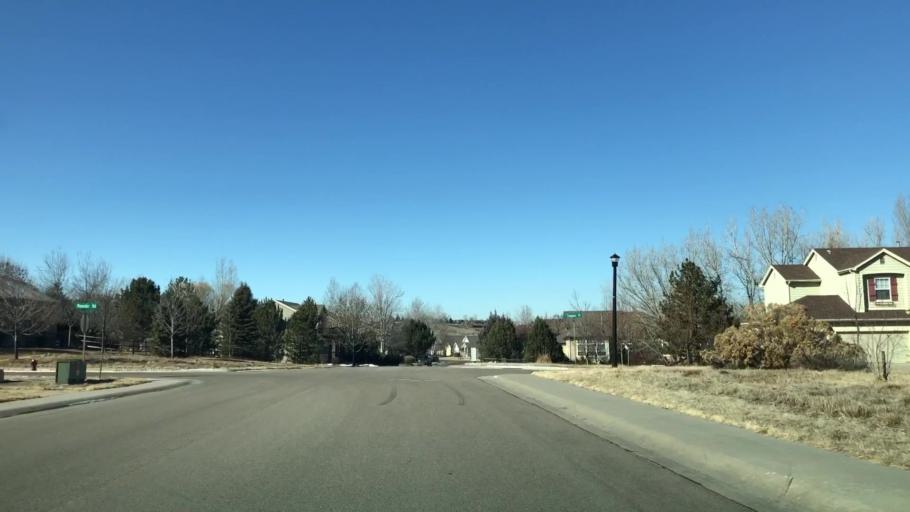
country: US
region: Colorado
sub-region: Weld County
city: Windsor
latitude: 40.4725
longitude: -104.9491
